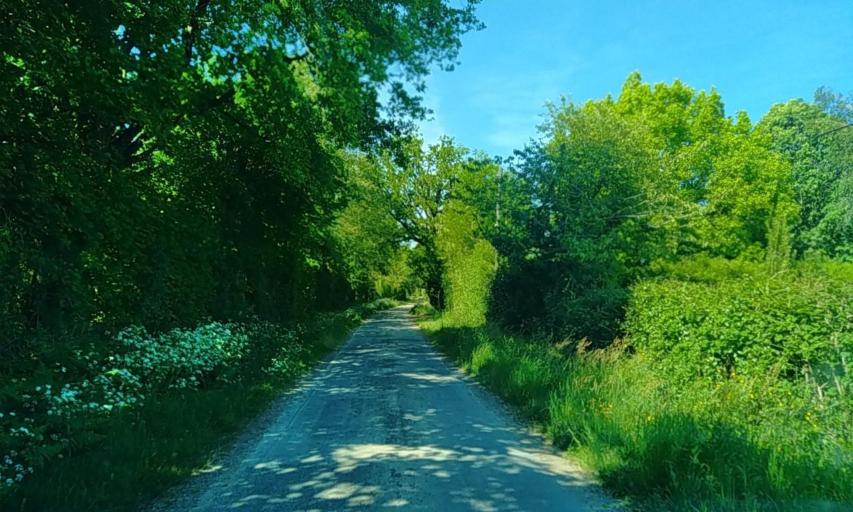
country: FR
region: Poitou-Charentes
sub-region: Departement des Deux-Sevres
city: Boisme
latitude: 46.7952
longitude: -0.4645
